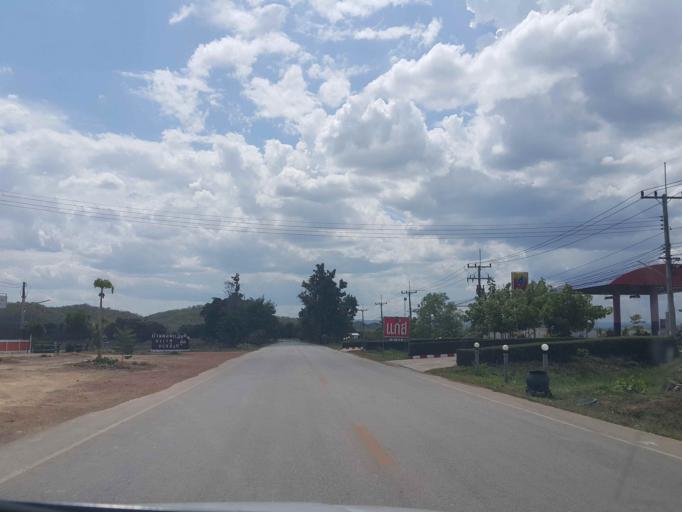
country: TH
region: Sukhothai
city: Thung Saliam
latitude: 17.3419
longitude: 99.6021
